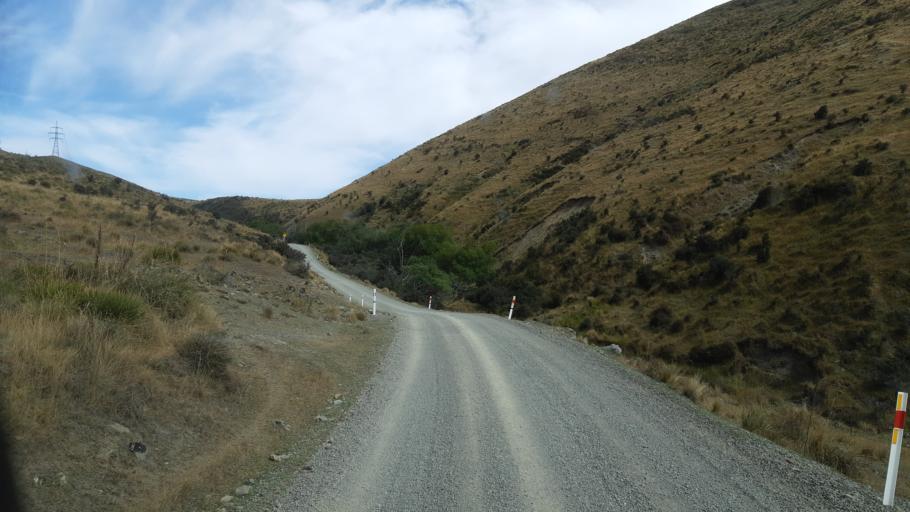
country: NZ
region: Canterbury
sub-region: Timaru District
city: Pleasant Point
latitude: -44.1926
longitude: 170.6204
